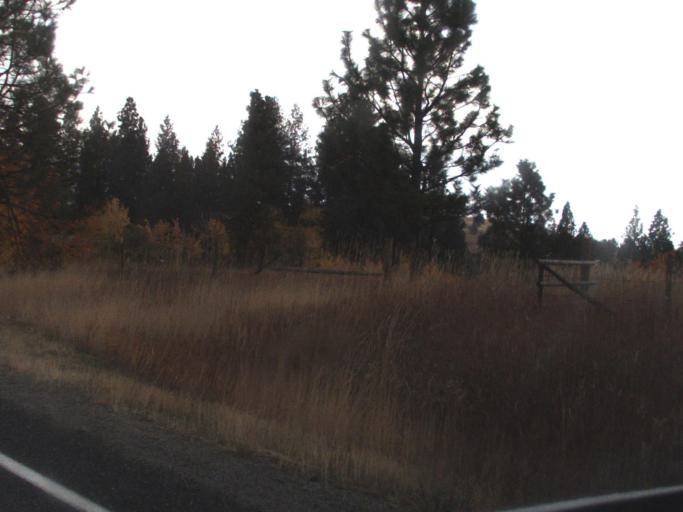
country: US
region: Washington
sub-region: Stevens County
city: Kettle Falls
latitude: 48.4523
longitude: -118.1755
